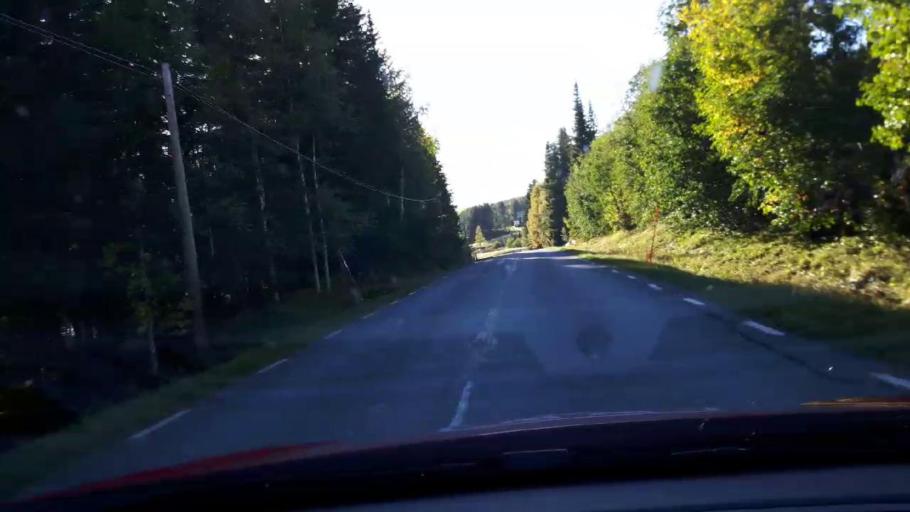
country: SE
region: Jaemtland
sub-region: OEstersunds Kommun
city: Lit
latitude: 63.8208
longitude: 14.8304
